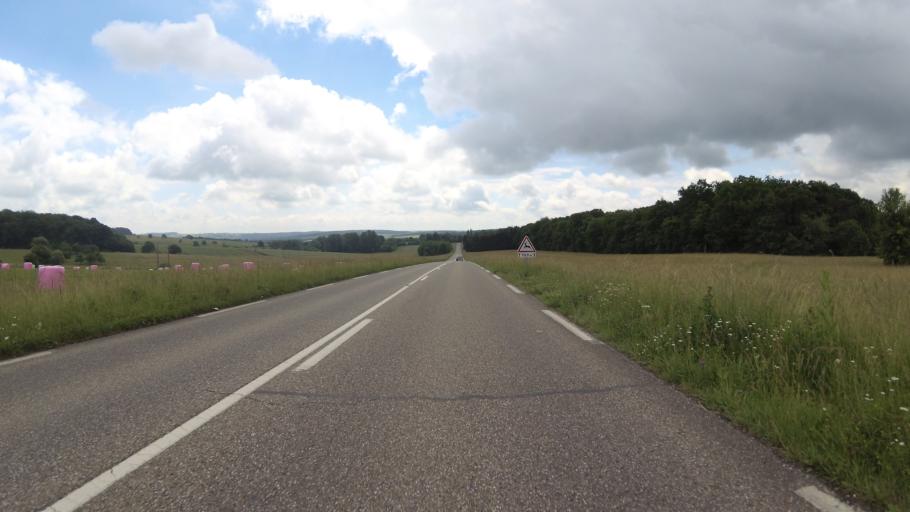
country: FR
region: Lorraine
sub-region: Departement de la Moselle
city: Remelfing
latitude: 49.0757
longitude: 7.0837
